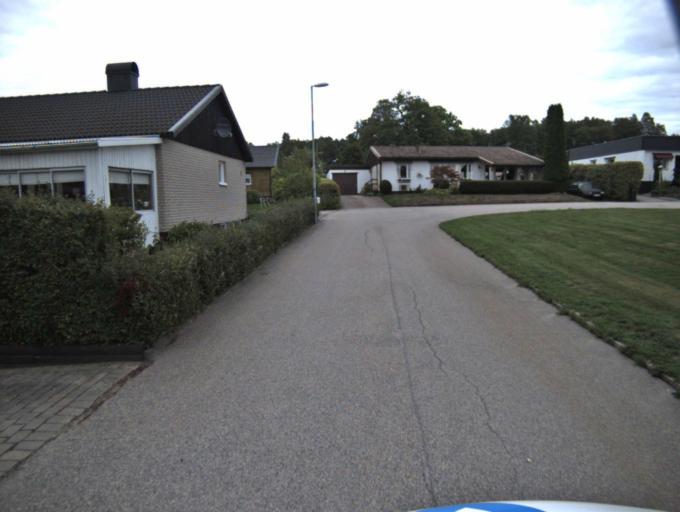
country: SE
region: Vaestra Goetaland
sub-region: Ulricehamns Kommun
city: Ulricehamn
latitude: 57.7984
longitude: 13.4319
